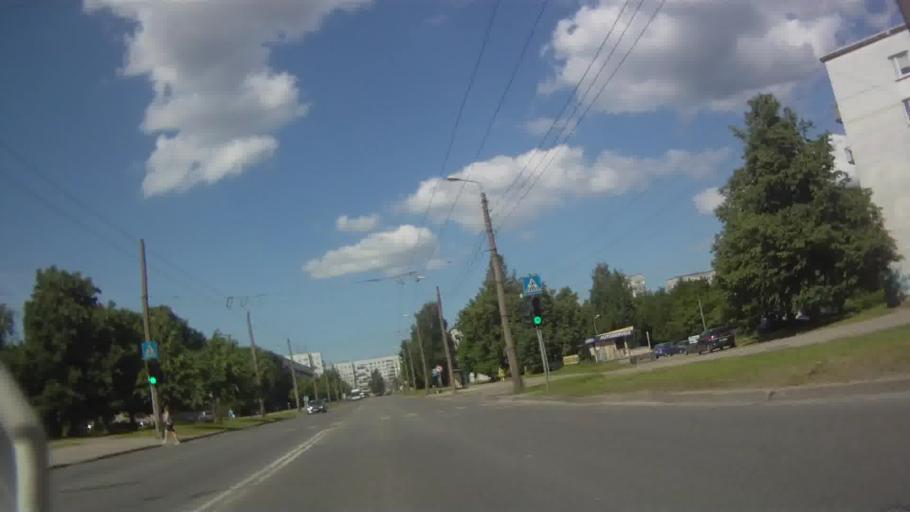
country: LV
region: Riga
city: Riga
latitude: 56.9549
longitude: 24.1755
